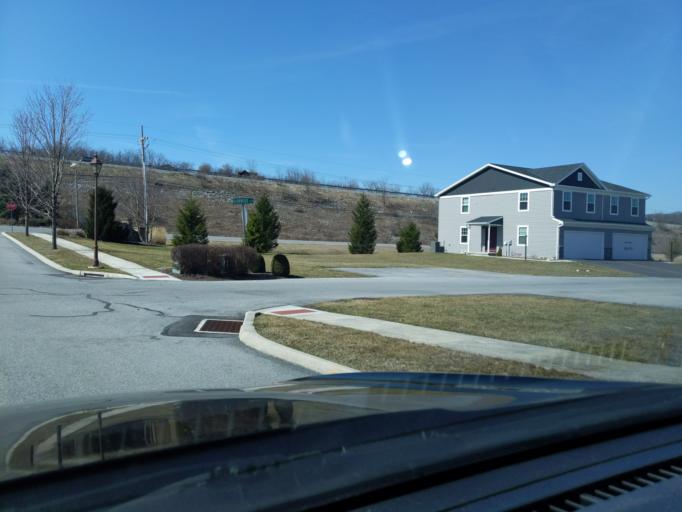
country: US
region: Pennsylvania
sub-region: Blair County
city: Duncansville
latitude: 40.4224
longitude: -78.4216
